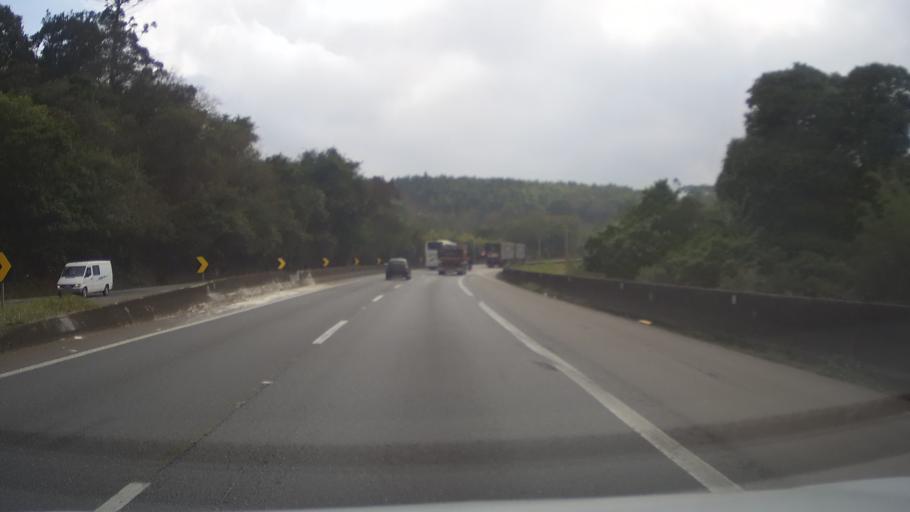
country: BR
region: Minas Gerais
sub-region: Extrema
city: Extrema
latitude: -22.8789
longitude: -46.3995
